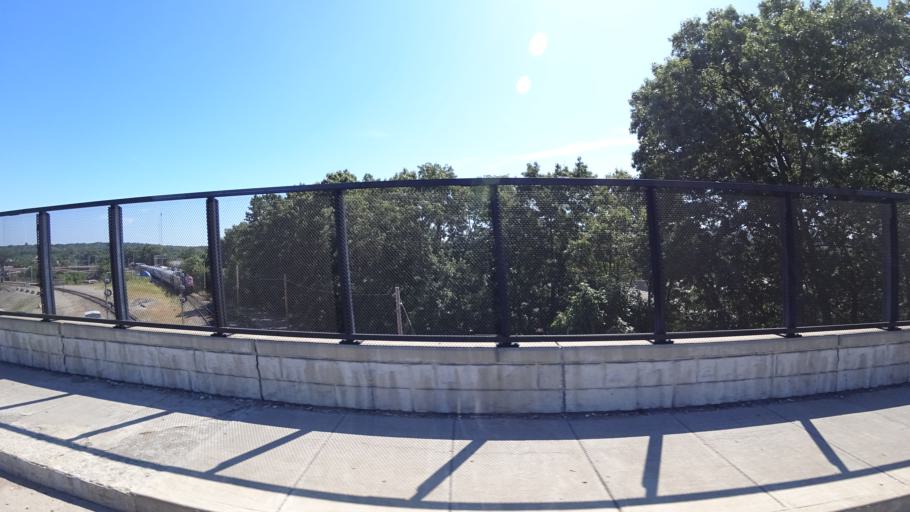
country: US
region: Massachusetts
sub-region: Norfolk County
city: Dedham
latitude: 42.2372
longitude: -71.1358
